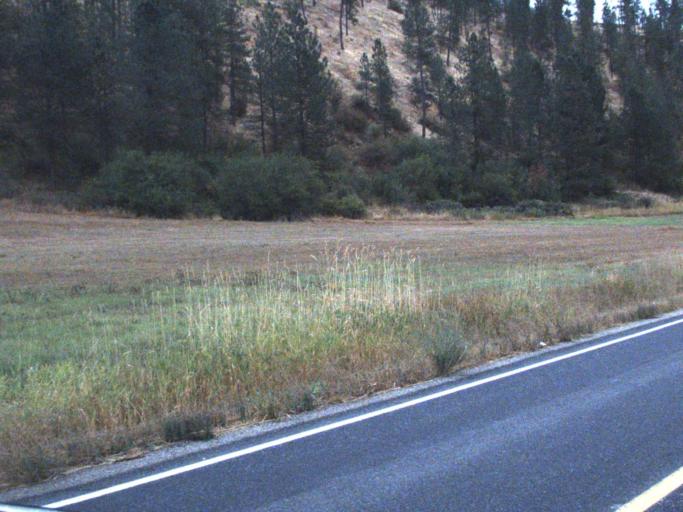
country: US
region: Washington
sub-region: Stevens County
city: Chewelah
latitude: 48.1827
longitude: -117.7303
